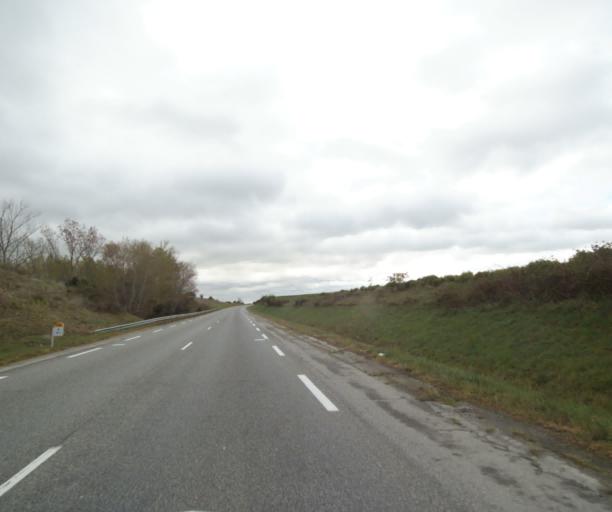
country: FR
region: Midi-Pyrenees
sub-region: Departement de l'Ariege
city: Saverdun
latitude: 43.2361
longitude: 1.5951
